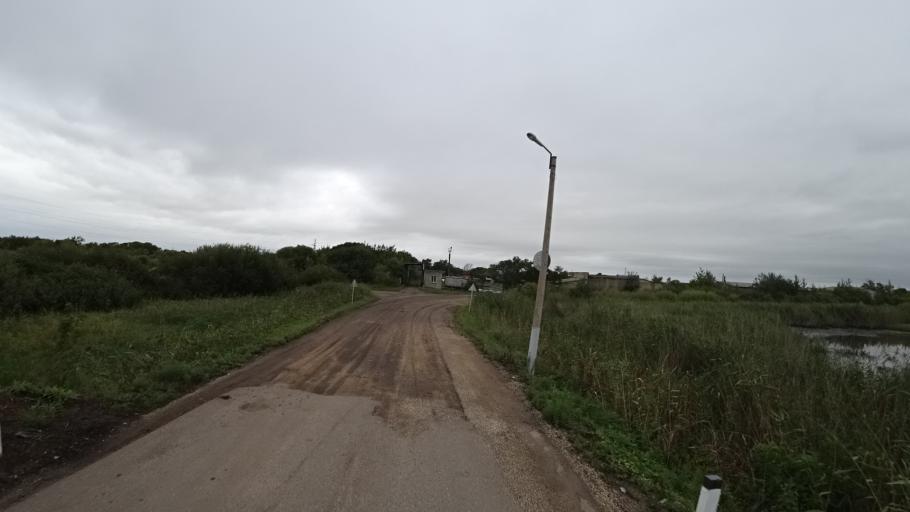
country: RU
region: Primorskiy
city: Chernigovka
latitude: 44.3335
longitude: 132.5231
